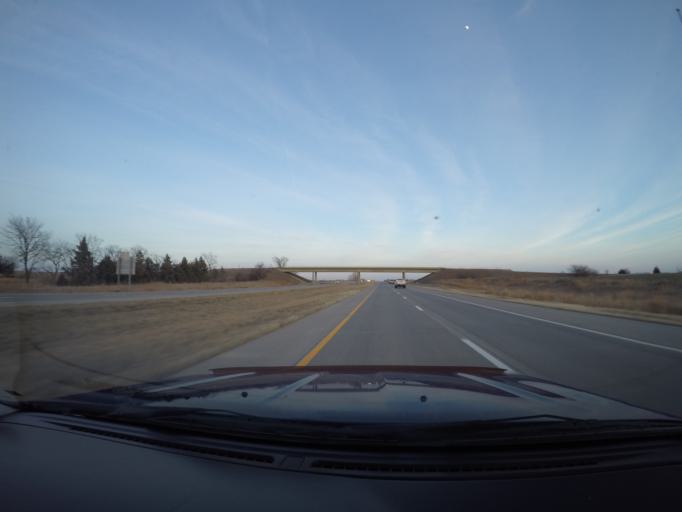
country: US
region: Kansas
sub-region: Dickinson County
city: Solomon
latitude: 38.9289
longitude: -97.3556
